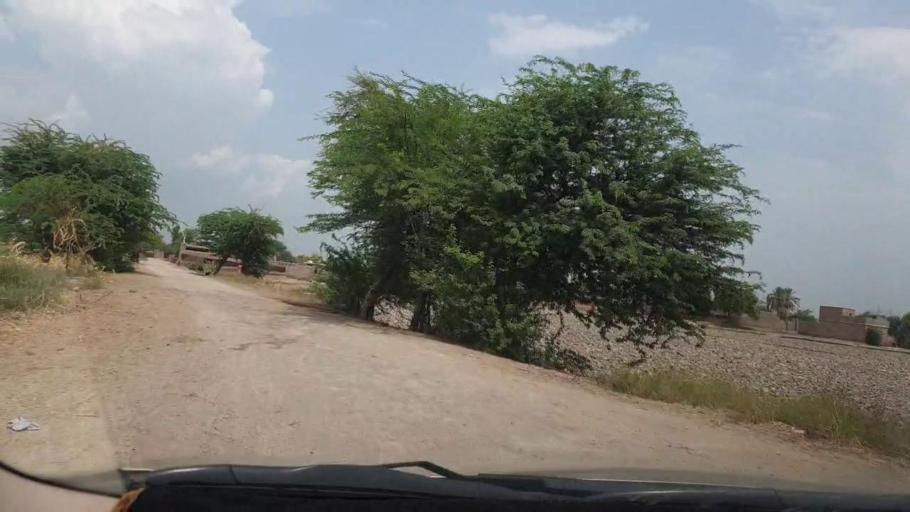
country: PK
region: Sindh
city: Larkana
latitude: 27.5627
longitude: 68.1249
